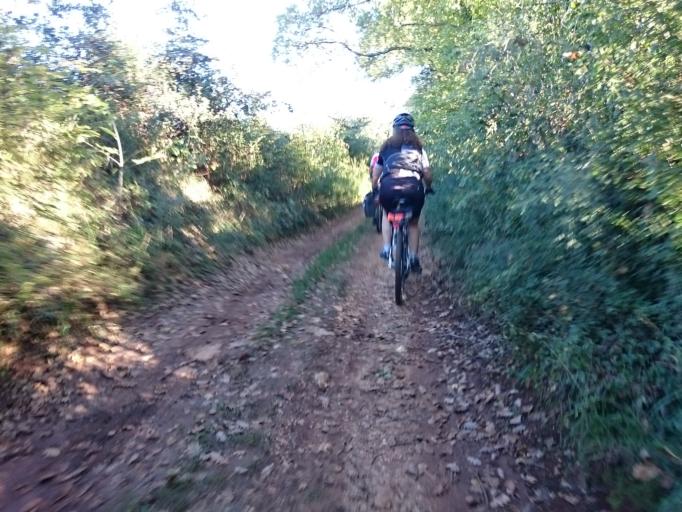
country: HR
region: Istarska
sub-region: Grad Porec
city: Porec
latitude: 45.2652
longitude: 13.6519
